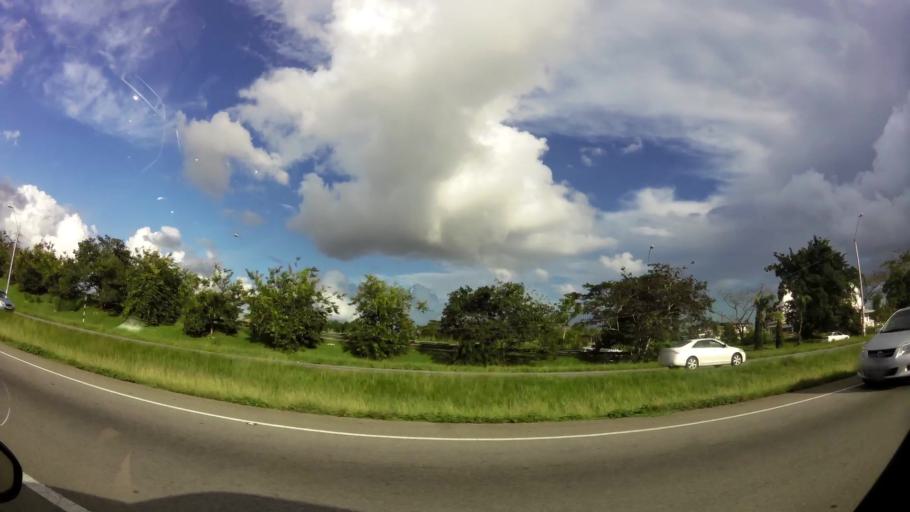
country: TT
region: Chaguanas
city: Chaguanas
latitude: 10.4820
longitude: -61.4054
